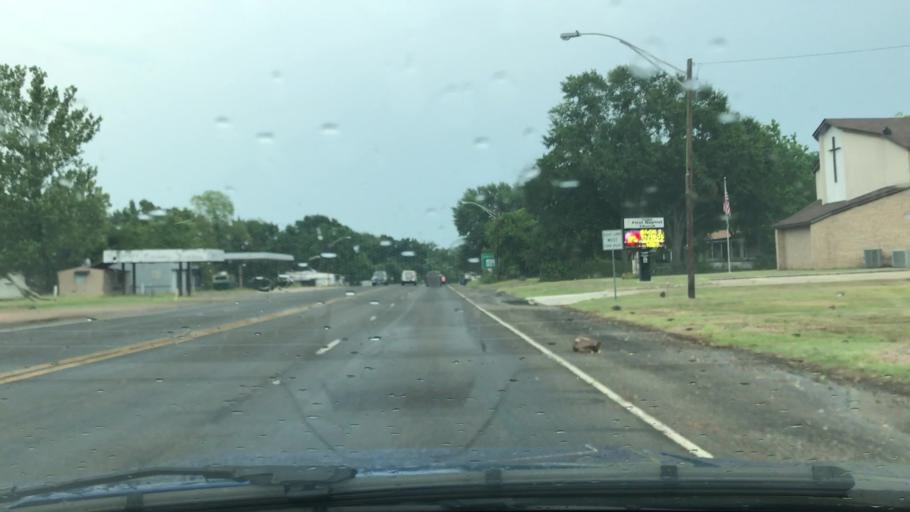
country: US
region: Texas
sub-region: Harrison County
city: Waskom
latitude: 32.4780
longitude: -94.0564
